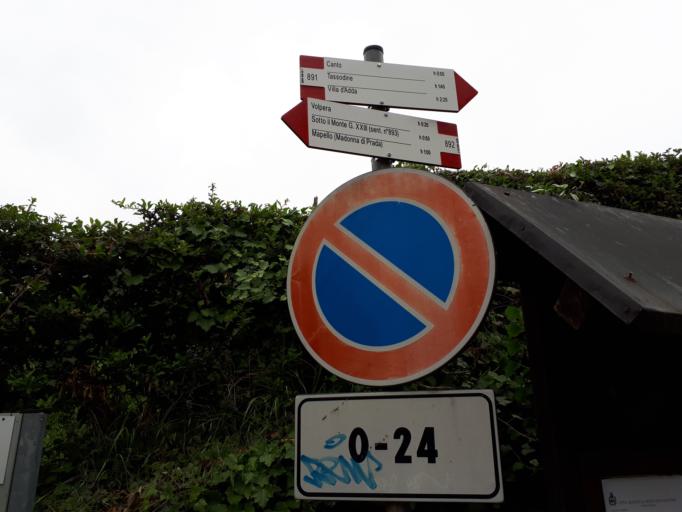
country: IT
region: Lombardy
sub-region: Provincia di Bergamo
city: Pontida
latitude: 45.7167
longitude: 9.5154
